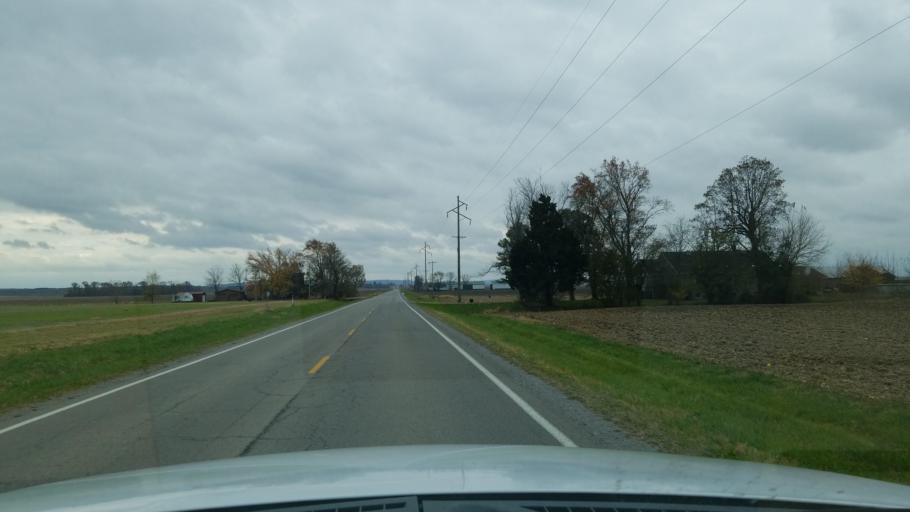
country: US
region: Illinois
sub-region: Saline County
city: Eldorado
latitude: 37.7886
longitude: -88.4382
